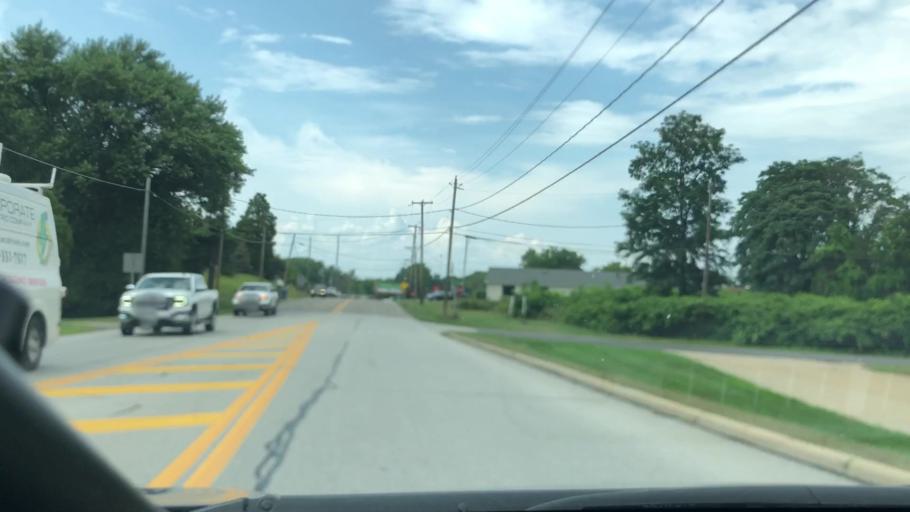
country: US
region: Ohio
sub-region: Summit County
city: Portage Lakes
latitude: 41.0184
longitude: -81.5245
